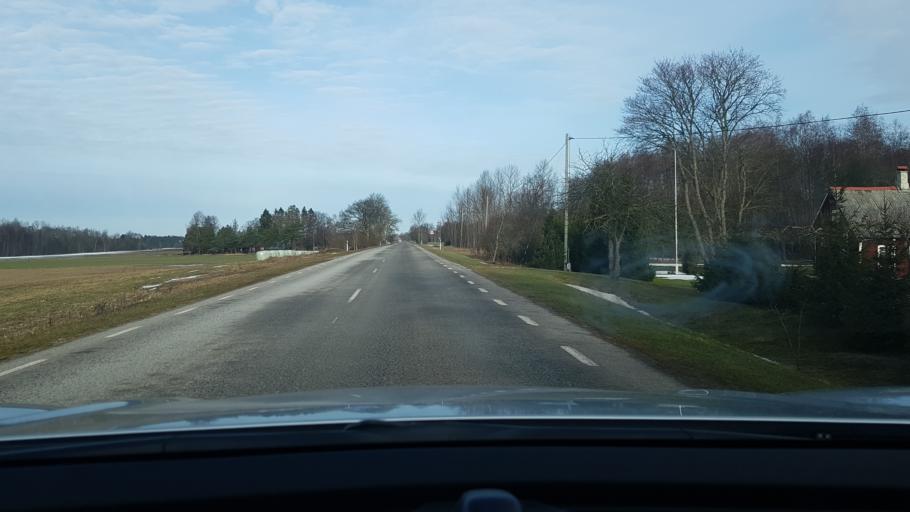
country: EE
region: Saare
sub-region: Kuressaare linn
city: Kuressaare
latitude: 58.4950
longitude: 22.7076
